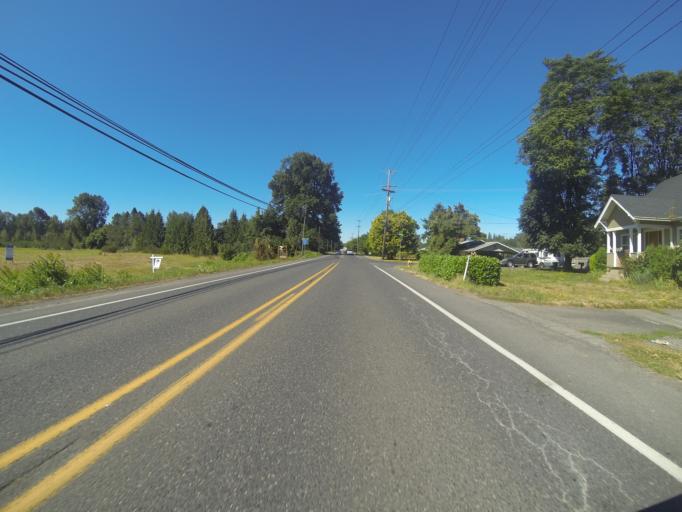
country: US
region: Washington
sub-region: Cowlitz County
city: Woodland
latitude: 45.9189
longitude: -122.7336
